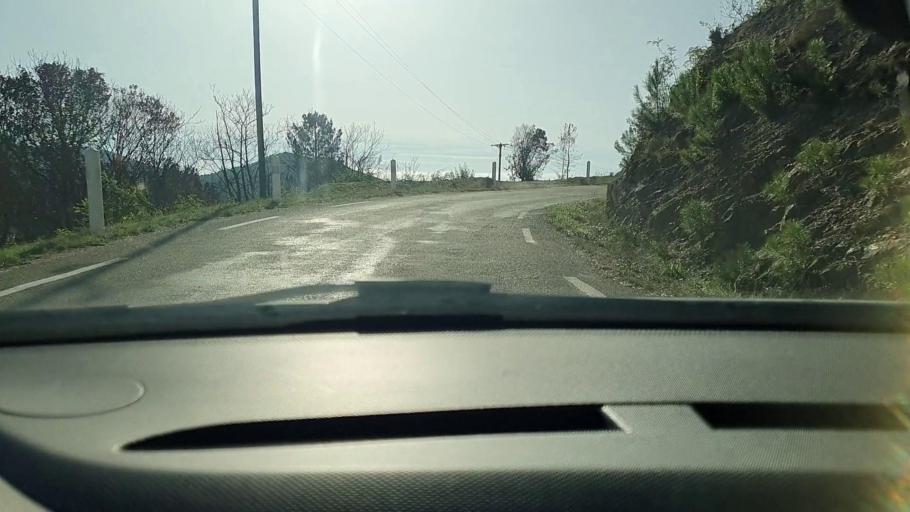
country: FR
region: Languedoc-Roussillon
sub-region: Departement du Gard
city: Besseges
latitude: 44.3090
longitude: 4.0888
